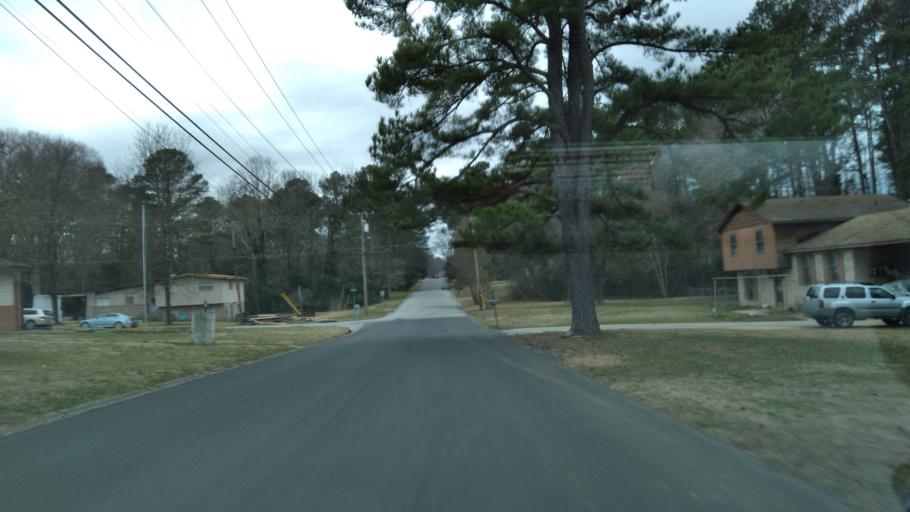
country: US
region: North Carolina
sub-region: Wake County
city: Garner
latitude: 35.7031
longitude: -78.6225
